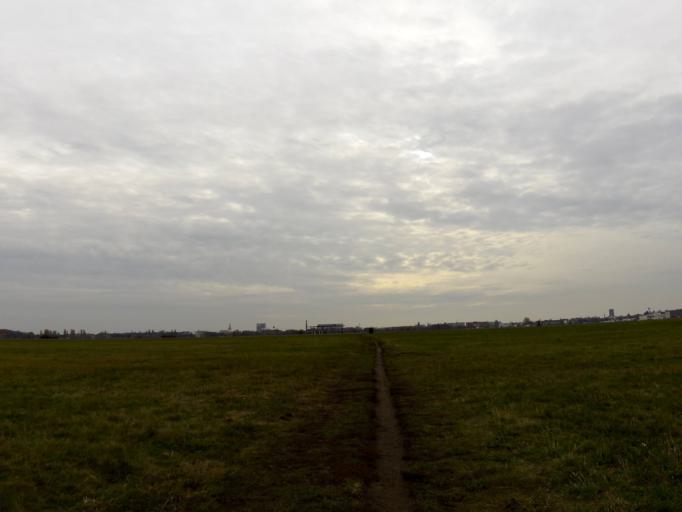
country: DE
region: Berlin
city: Tempelhof Bezirk
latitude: 52.4765
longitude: 13.4050
